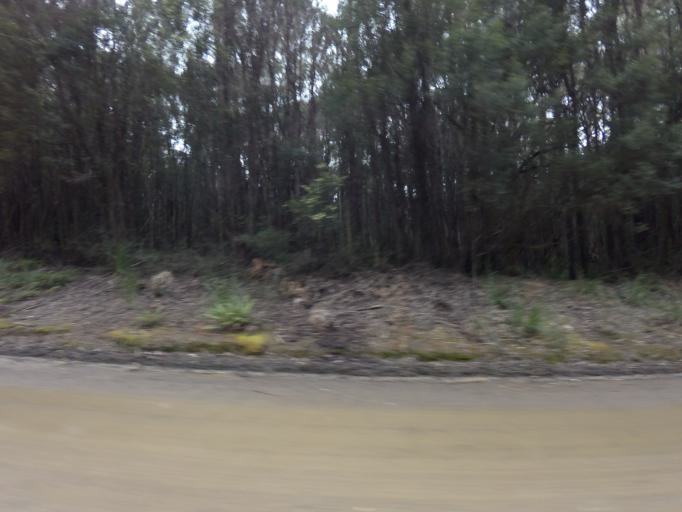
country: AU
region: Tasmania
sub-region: Huon Valley
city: Geeveston
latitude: -43.4043
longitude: 146.8664
